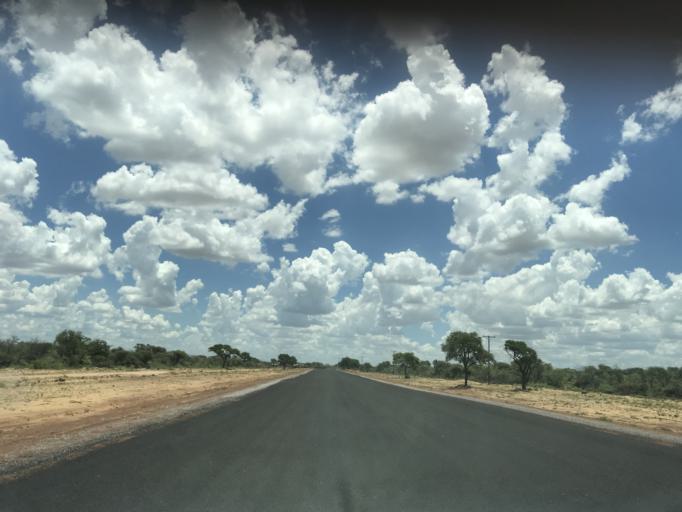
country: BW
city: Mabuli
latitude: -25.7964
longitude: 24.6670
